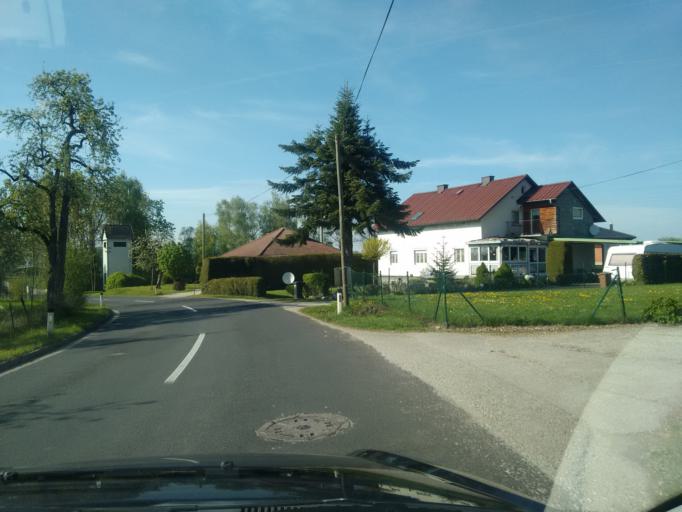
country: AT
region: Upper Austria
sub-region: Wels-Land
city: Holzhausen
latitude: 48.2061
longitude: 14.0923
